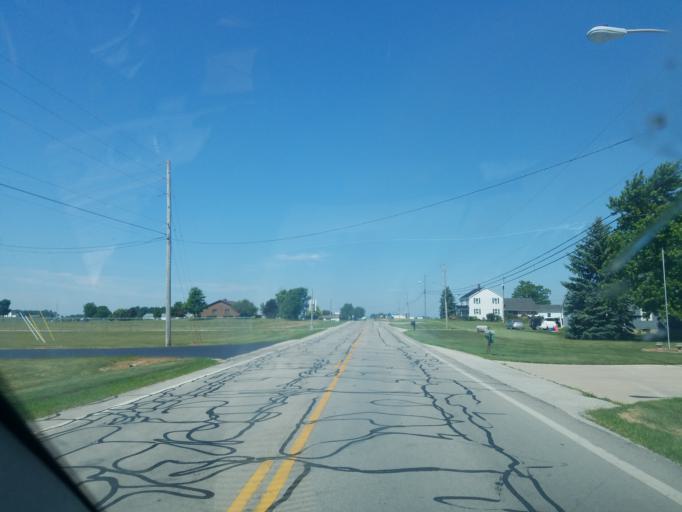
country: US
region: Ohio
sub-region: Auglaize County
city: New Bremen
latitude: 40.4076
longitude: -84.4961
